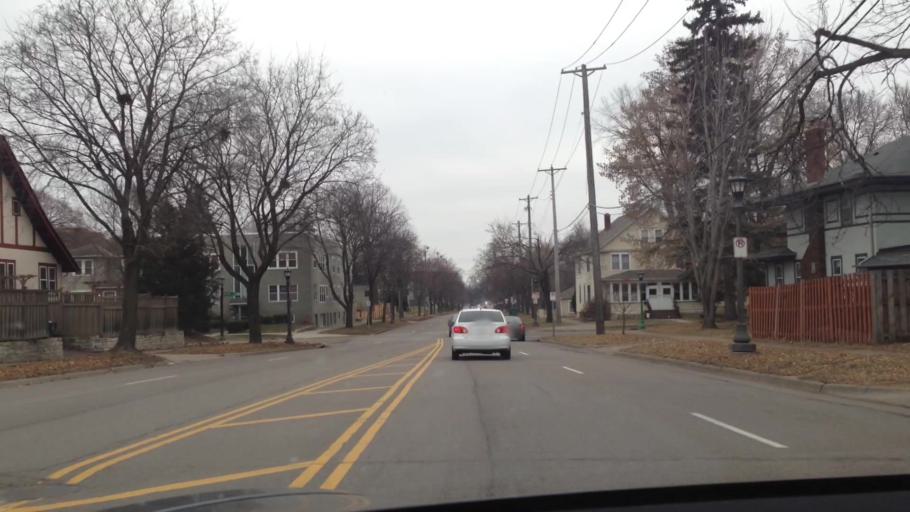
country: US
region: Minnesota
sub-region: Ramsey County
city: Falcon Heights
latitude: 44.9479
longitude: -93.1925
